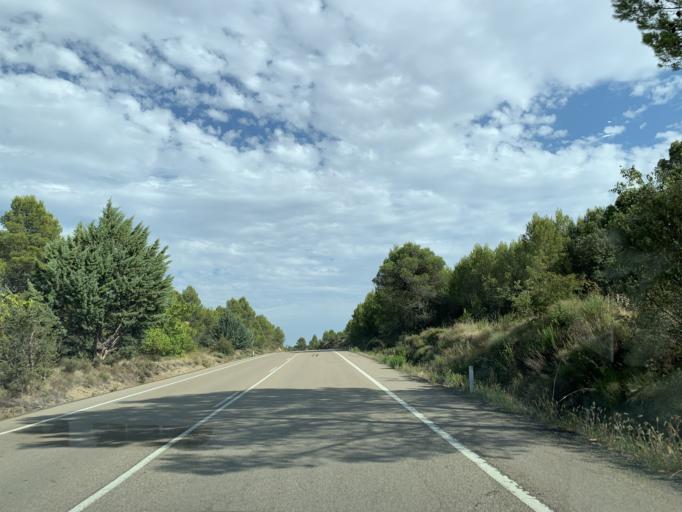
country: ES
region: Aragon
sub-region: Provincia de Zaragoza
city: Santa Eulalia de Gallego
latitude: 42.3032
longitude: -0.7409
